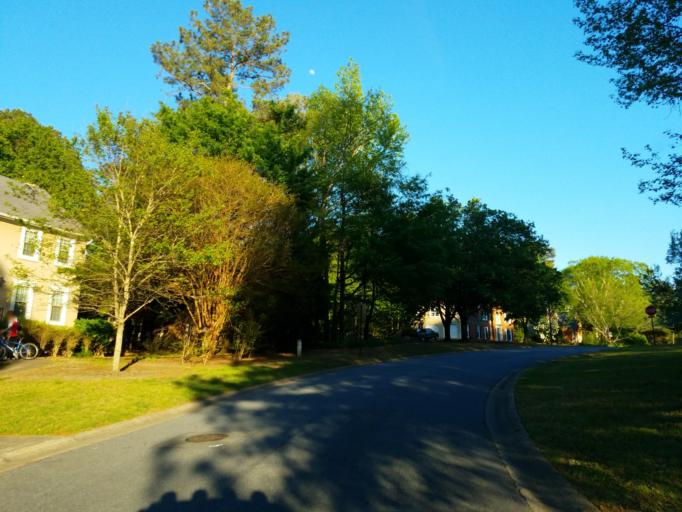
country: US
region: Georgia
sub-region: Cobb County
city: Powder Springs
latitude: 33.9217
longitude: -84.6416
